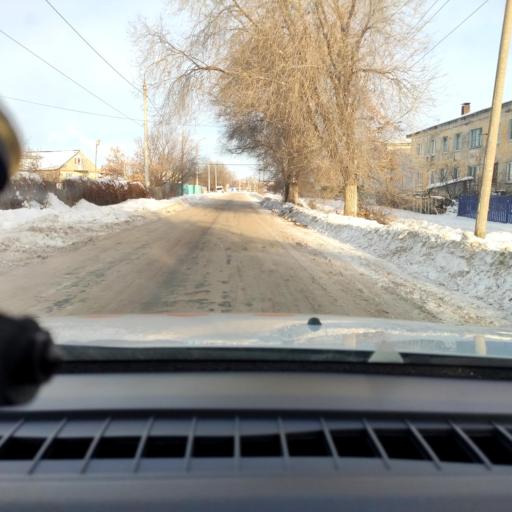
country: RU
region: Samara
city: Samara
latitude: 53.1370
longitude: 50.2394
